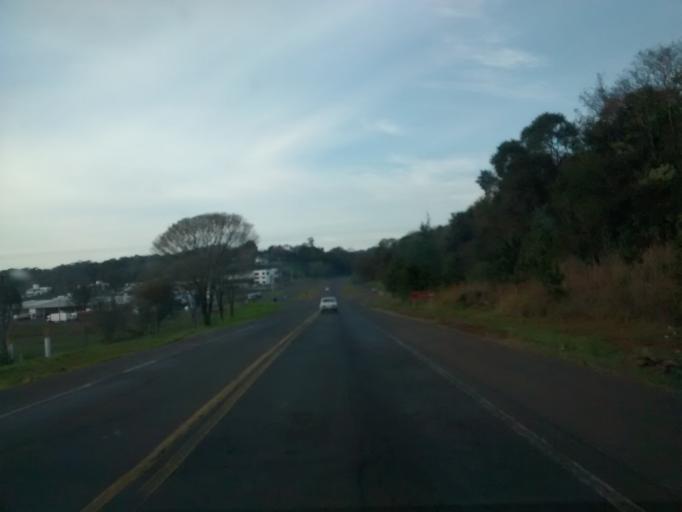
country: BR
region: Parana
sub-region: Francisco Beltrao
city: Francisco Beltrao
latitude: -26.1002
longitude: -53.0594
